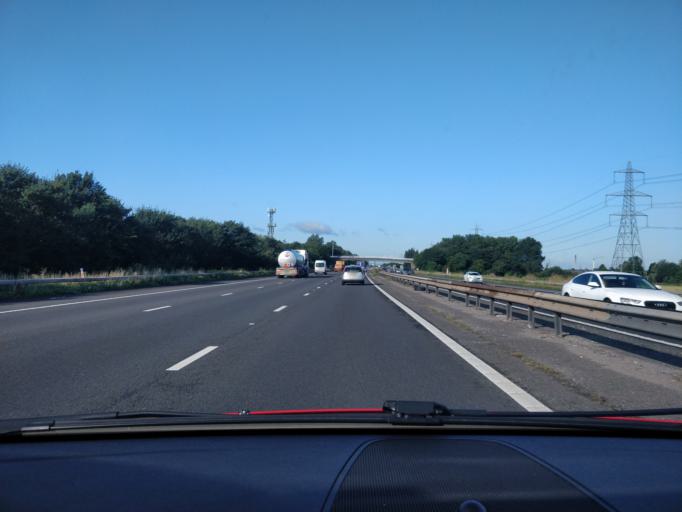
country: GB
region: England
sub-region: Cheshire West and Chester
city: Helsby
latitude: 53.2792
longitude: -2.7699
